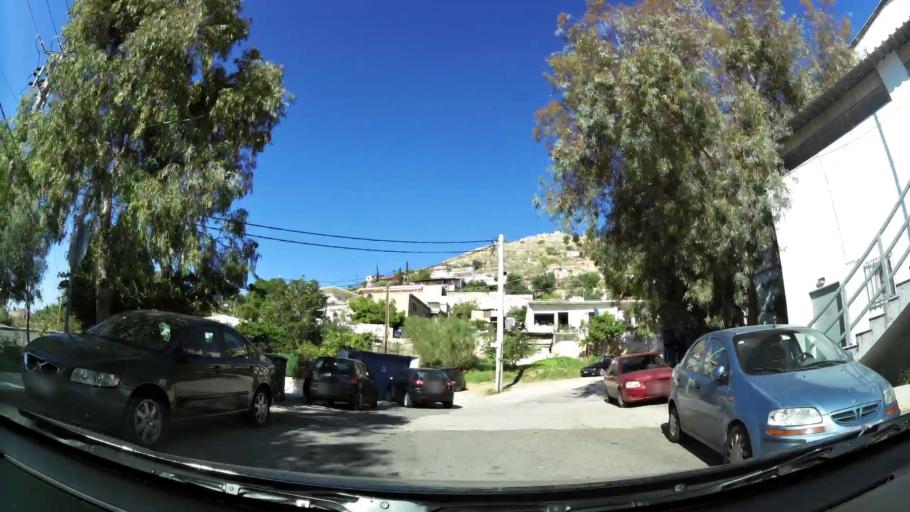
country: GR
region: Attica
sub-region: Nomos Piraios
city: Keratsini
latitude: 37.9639
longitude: 23.5964
